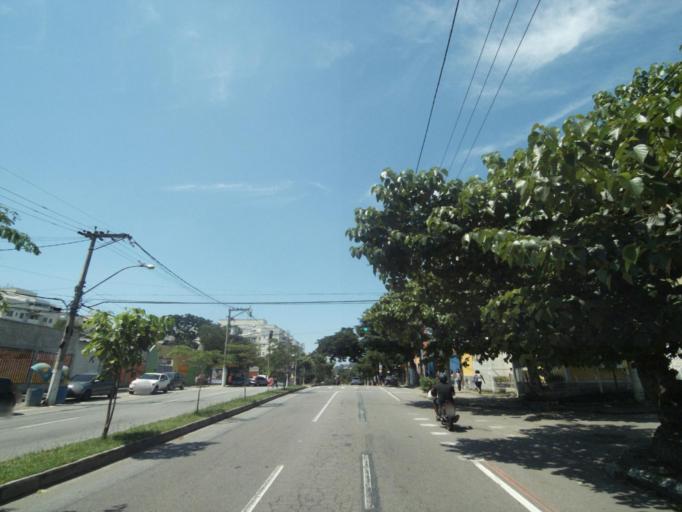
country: BR
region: Rio de Janeiro
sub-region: Niteroi
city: Niteroi
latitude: -22.9074
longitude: -43.0617
